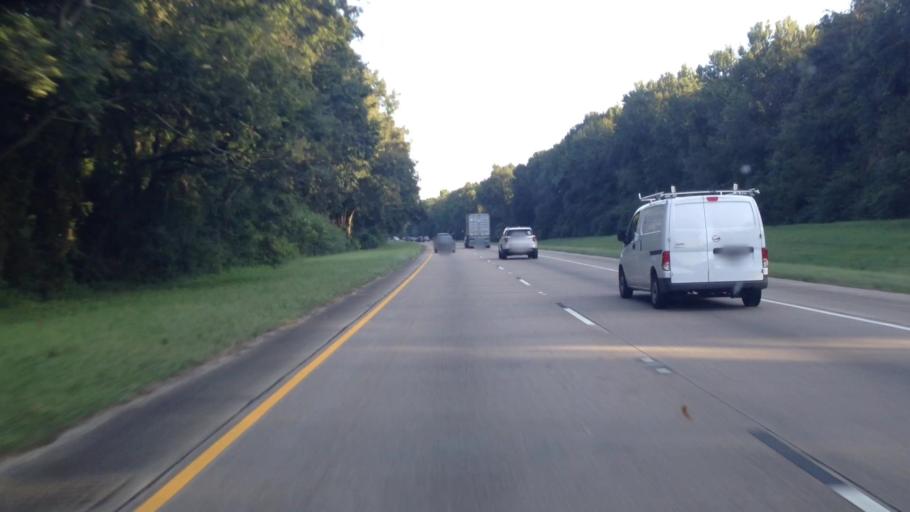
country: US
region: Louisiana
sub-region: Ascension Parish
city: Prairieville
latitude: 30.3074
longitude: -90.9941
